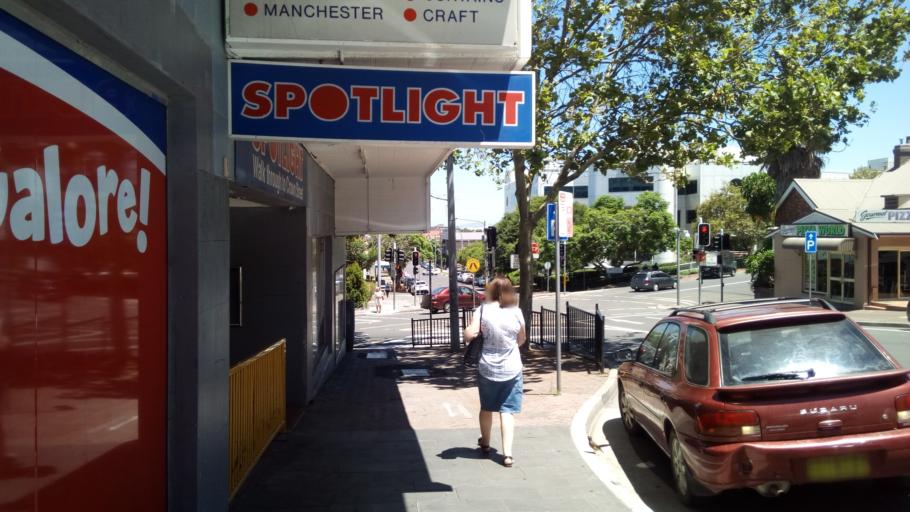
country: AU
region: New South Wales
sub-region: Wollongong
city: Wollongong
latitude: -34.4257
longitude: 150.8910
